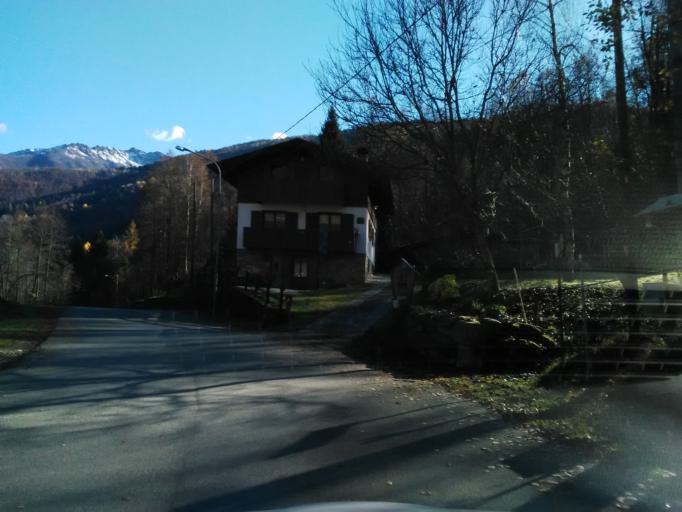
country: IT
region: Piedmont
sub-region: Provincia di Vercelli
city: Pila
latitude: 45.7683
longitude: 8.0773
